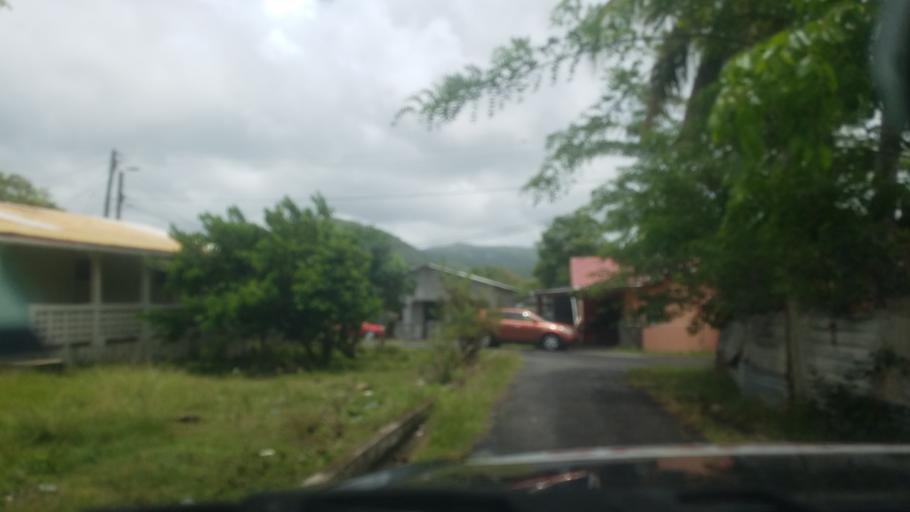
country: LC
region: Laborie Quarter
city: Laborie
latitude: 13.7429
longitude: -60.9600
